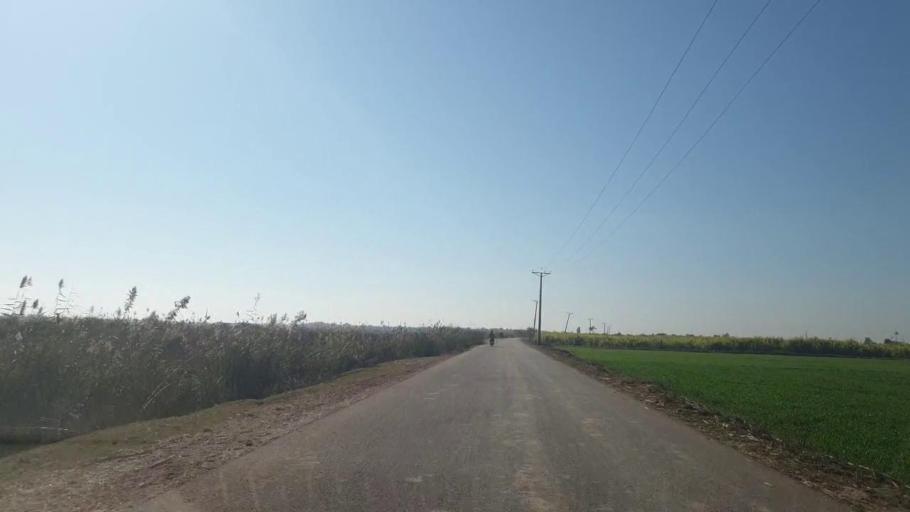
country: PK
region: Sindh
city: Kot Diji
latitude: 27.3071
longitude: 68.6462
